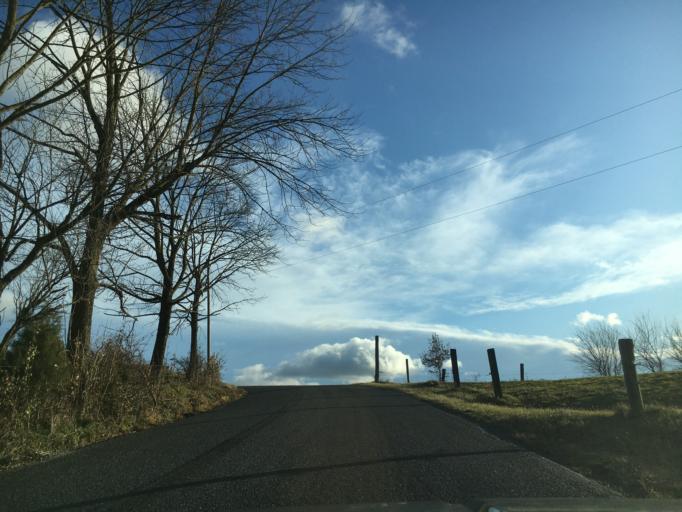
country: US
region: Pennsylvania
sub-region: Carbon County
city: Lehighton
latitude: 40.8037
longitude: -75.7326
